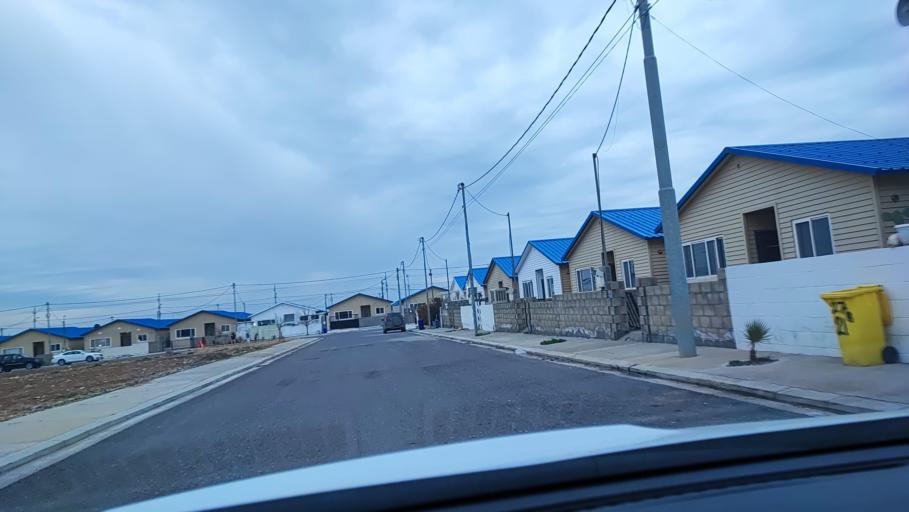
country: IQ
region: Arbil
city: Erbil
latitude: 36.2866
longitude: 44.0801
